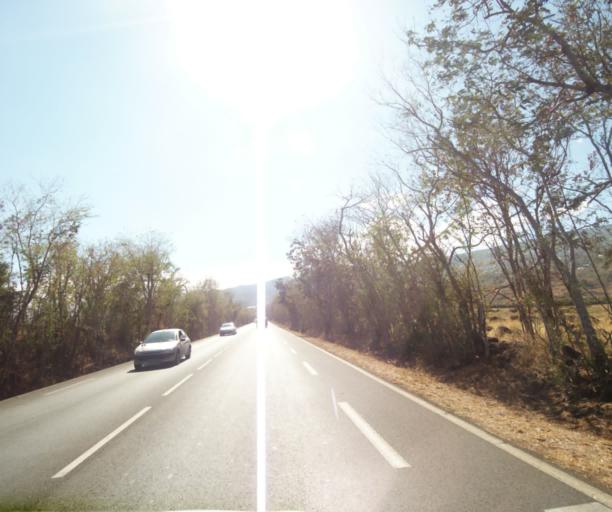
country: RE
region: Reunion
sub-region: Reunion
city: Saint-Paul
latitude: -20.9823
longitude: 55.3068
